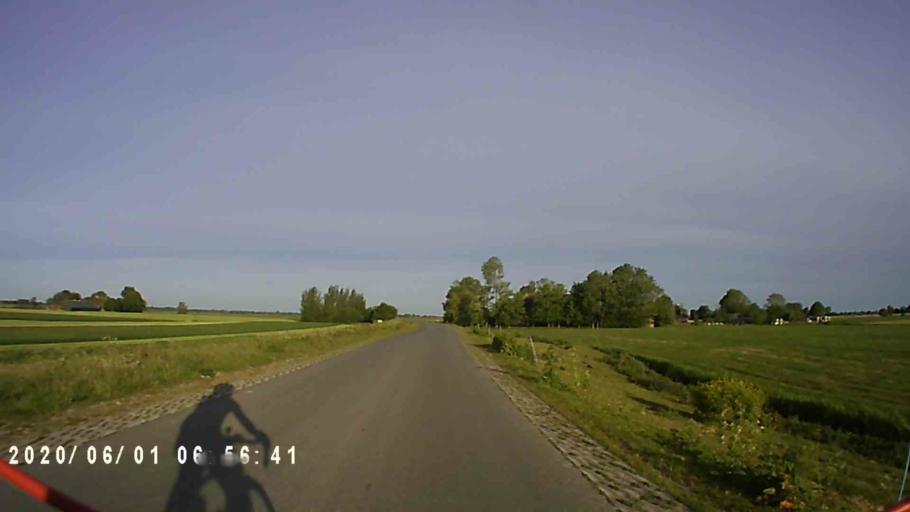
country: NL
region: Friesland
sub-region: Gemeente Kollumerland en Nieuwkruisland
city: Kollum
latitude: 53.3166
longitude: 6.1108
